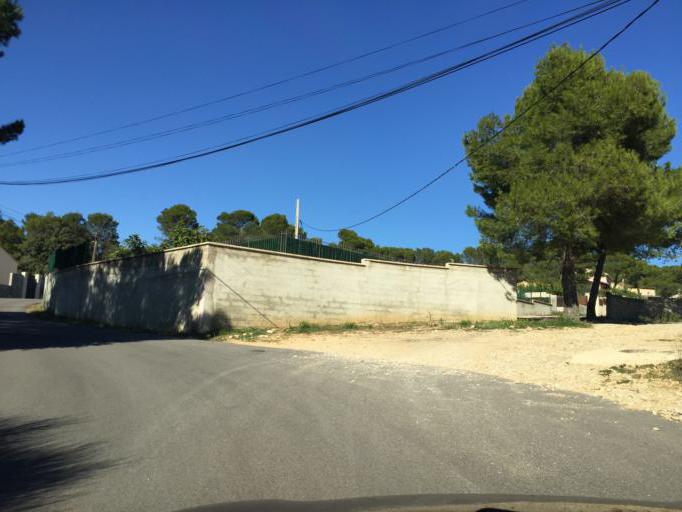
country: FR
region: Provence-Alpes-Cote d'Azur
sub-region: Departement du Vaucluse
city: Piolenc
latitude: 44.1979
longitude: 4.7535
